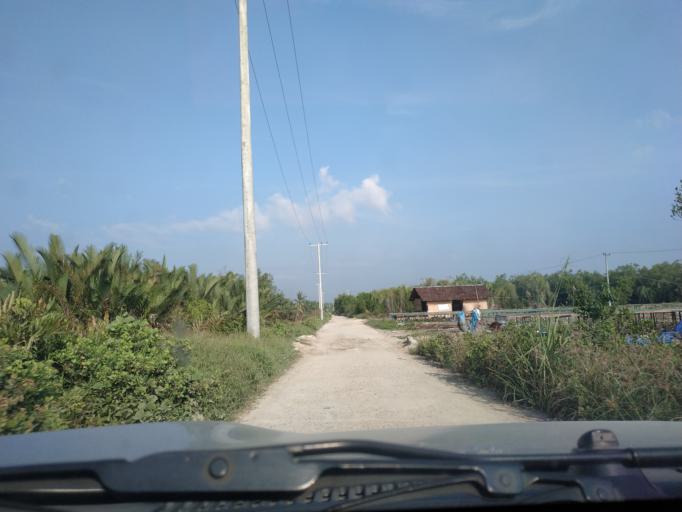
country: ID
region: North Sumatra
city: Teluk Nibung
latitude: 3.1018
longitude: 99.7766
